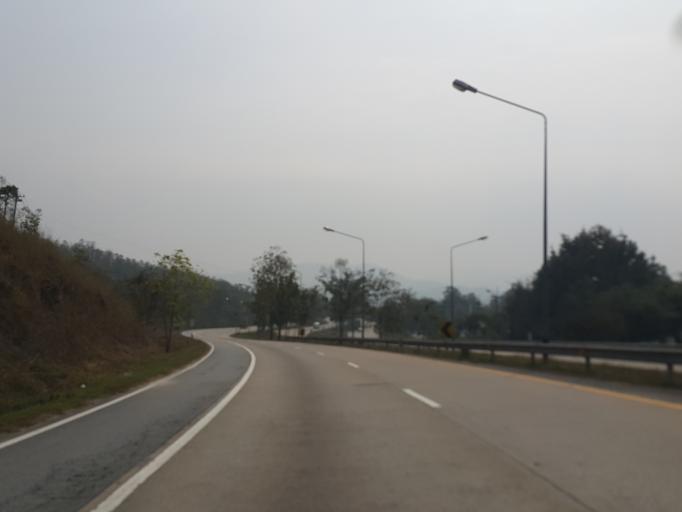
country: TH
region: Lamphun
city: Mae Tha
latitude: 18.4645
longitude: 99.1291
